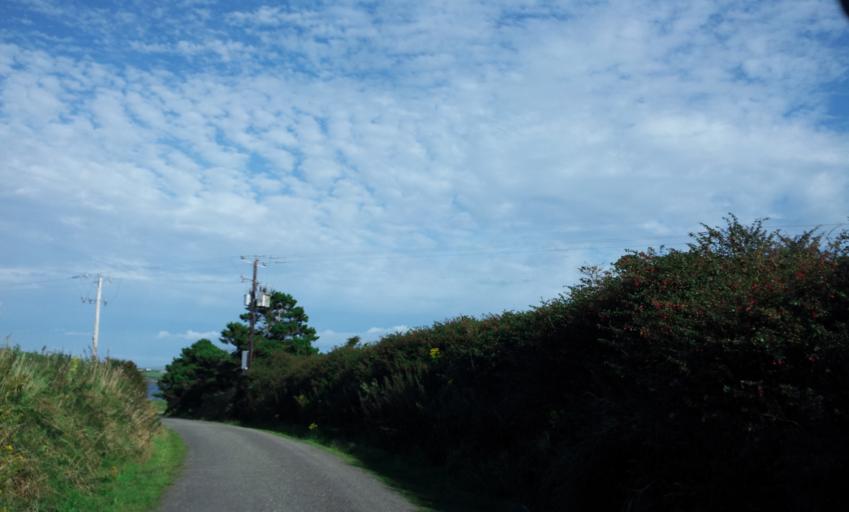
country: IE
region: Munster
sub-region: Ciarrai
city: Dingle
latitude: 52.1274
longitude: -10.3796
